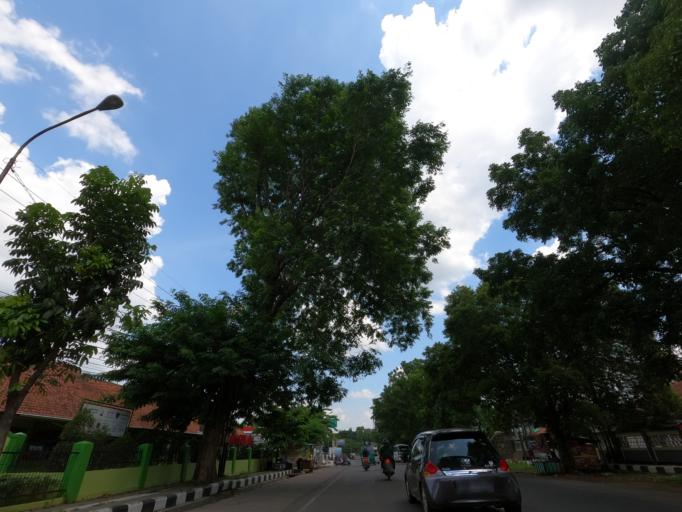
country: ID
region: West Java
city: Pamanukan
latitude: -6.5551
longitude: 107.7597
